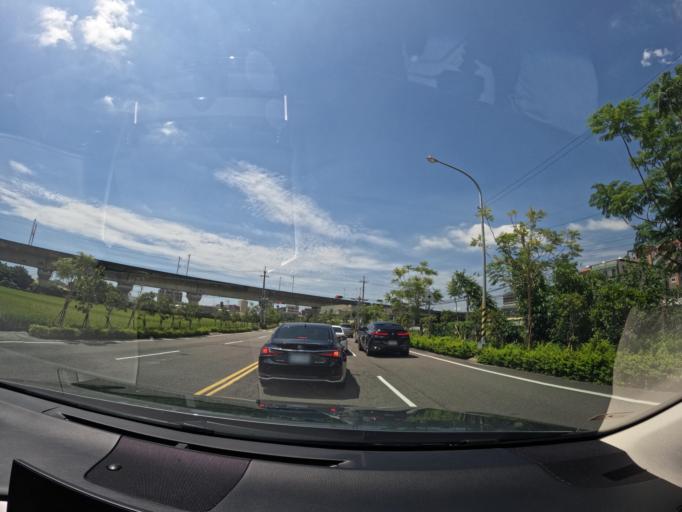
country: TW
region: Taiwan
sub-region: Hsinchu
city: Hsinchu
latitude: 24.6821
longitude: 120.9319
